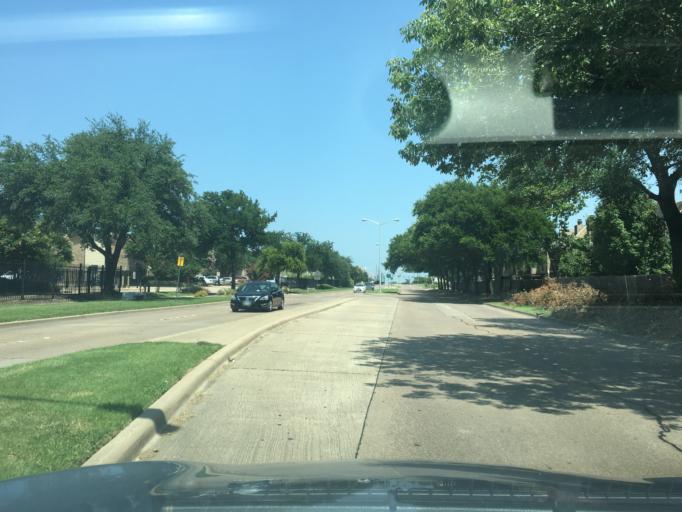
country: US
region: Texas
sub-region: Dallas County
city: Richardson
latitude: 32.9166
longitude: -96.7050
